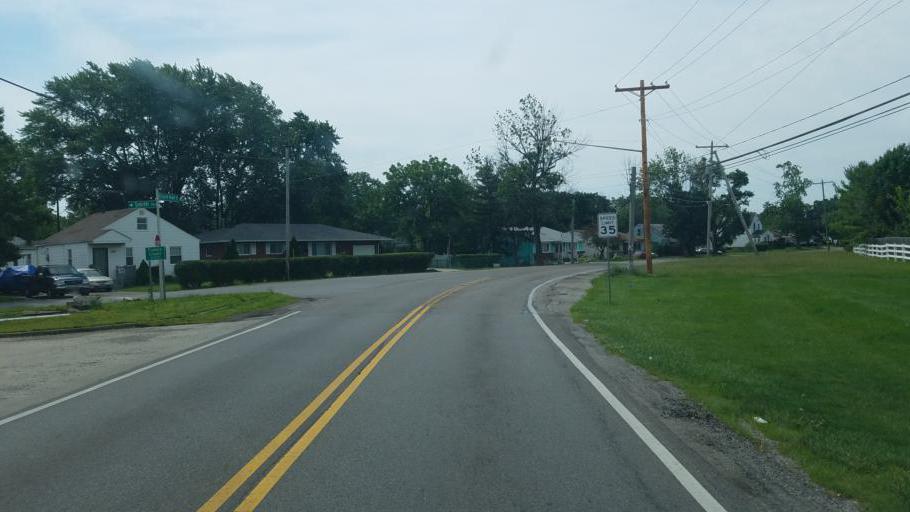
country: US
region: Ohio
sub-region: Franklin County
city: Lincoln Village
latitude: 39.9580
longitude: -83.1453
